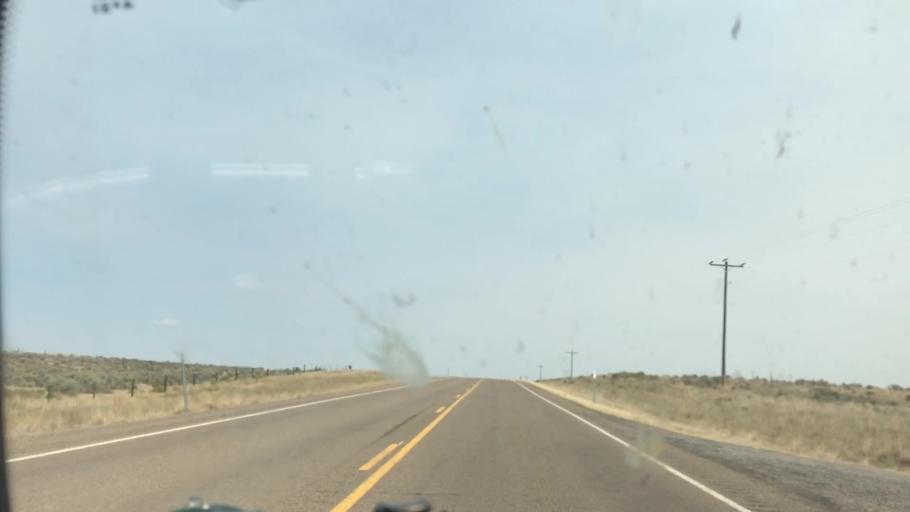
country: US
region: Idaho
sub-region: Owyhee County
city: Homedale
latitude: 42.8572
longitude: -117.5706
